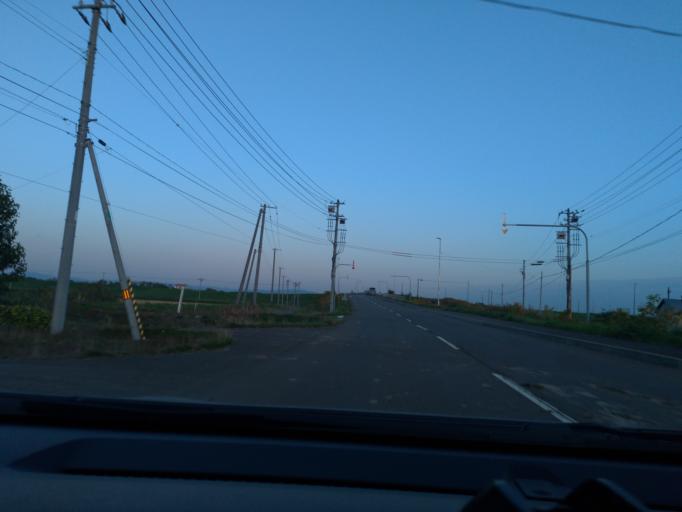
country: JP
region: Hokkaido
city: Iwamizawa
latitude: 43.3346
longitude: 141.6873
